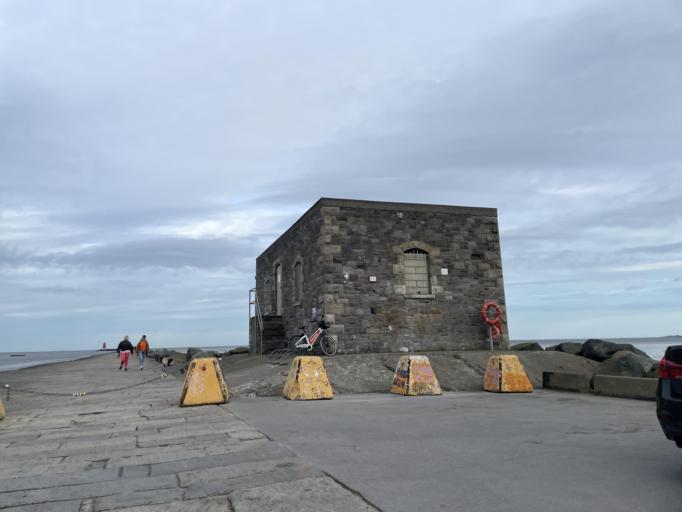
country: IE
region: Leinster
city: Dollymount
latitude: 53.3409
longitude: -6.1770
